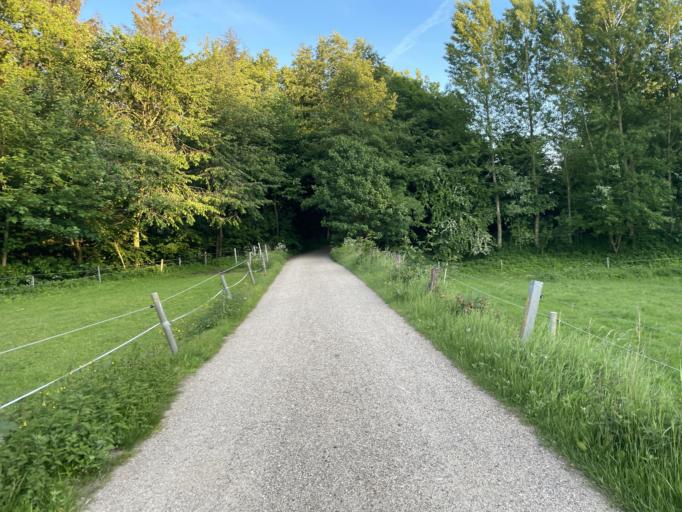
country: DE
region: Schleswig-Holstein
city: Husum
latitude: 54.4717
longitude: 9.0717
